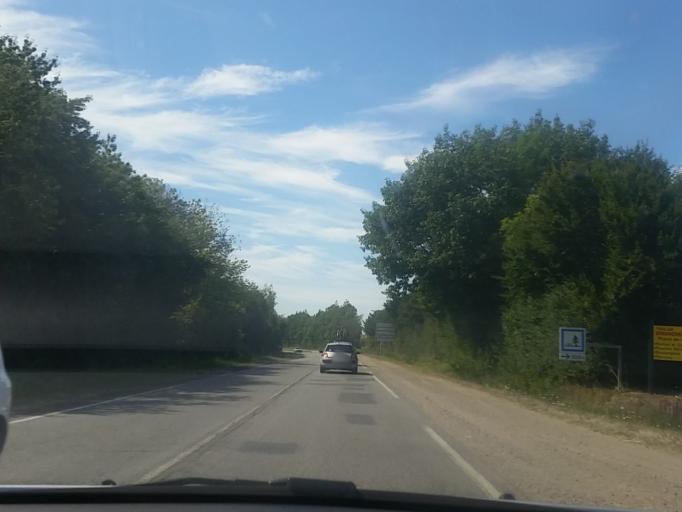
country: FR
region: Pays de la Loire
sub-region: Departement de la Loire-Atlantique
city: Saint-Pere-en-Retz
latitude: 47.1992
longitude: -2.0338
